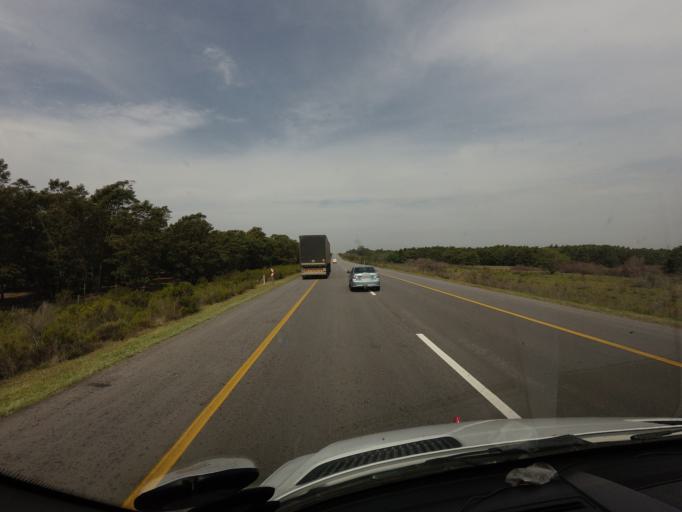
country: ZA
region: Eastern Cape
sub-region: Cacadu District Municipality
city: Kruisfontein
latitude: -33.9954
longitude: 24.7398
